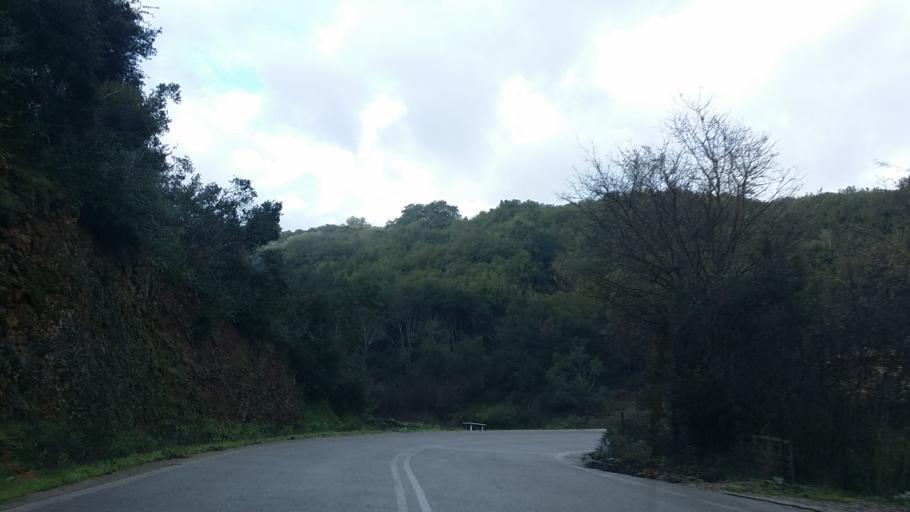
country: GR
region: West Greece
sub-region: Nomos Aitolias kai Akarnanias
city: Katouna
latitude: 38.7786
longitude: 21.1250
